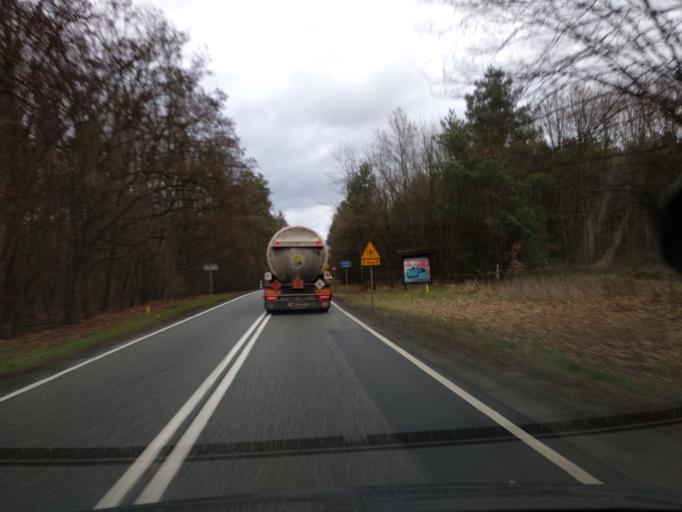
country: PL
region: Lower Silesian Voivodeship
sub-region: Powiat olesnicki
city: Twardogora
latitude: 51.3014
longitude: 17.5365
